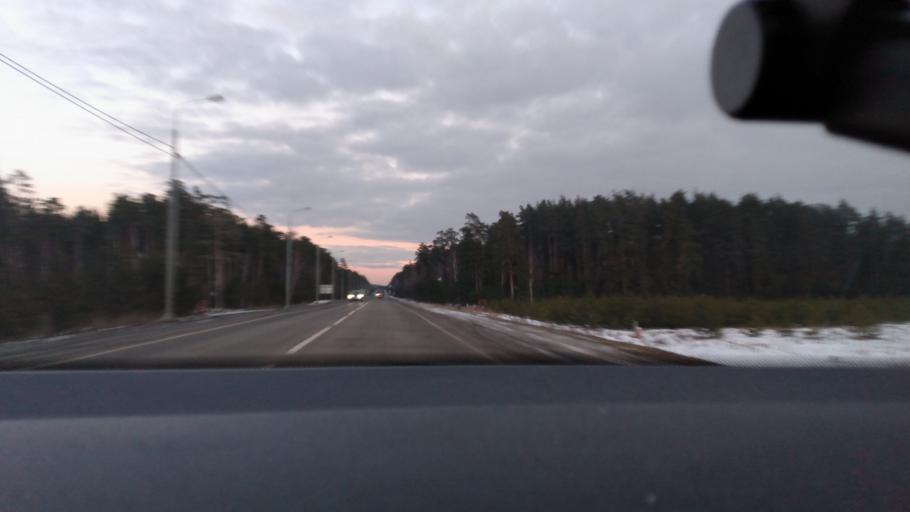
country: RU
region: Moskovskaya
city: Il'inskiy Pogost
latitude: 55.4886
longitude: 38.8841
